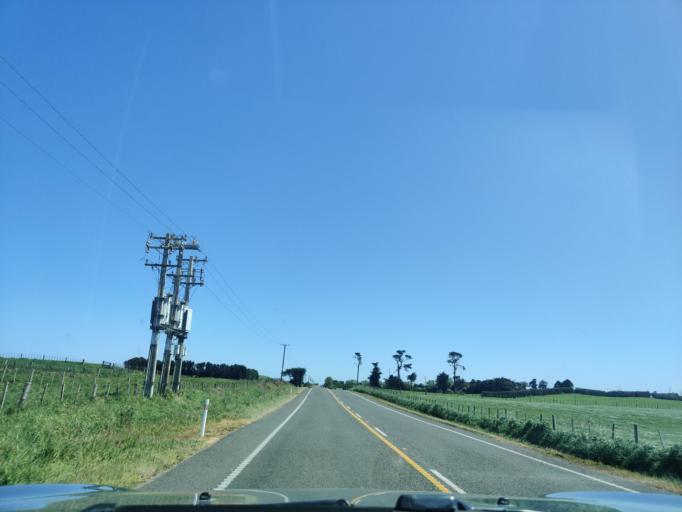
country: NZ
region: Taranaki
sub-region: South Taranaki District
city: Patea
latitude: -39.7763
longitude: 174.6829
